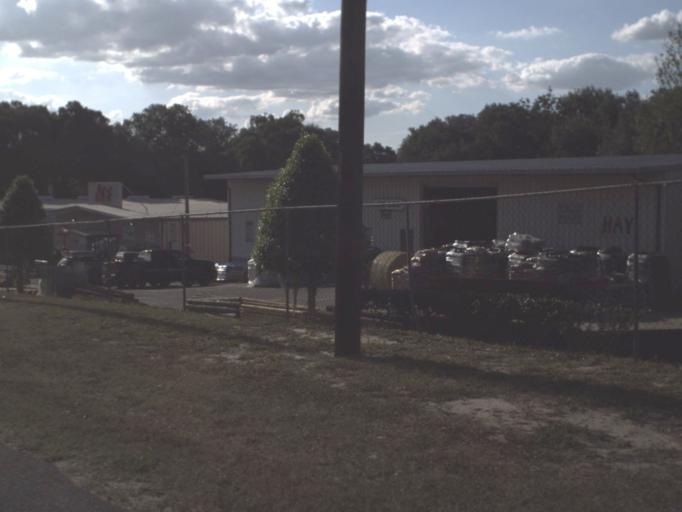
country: US
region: Florida
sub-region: Lake County
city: Mount Plymouth
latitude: 28.8079
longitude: -81.5536
